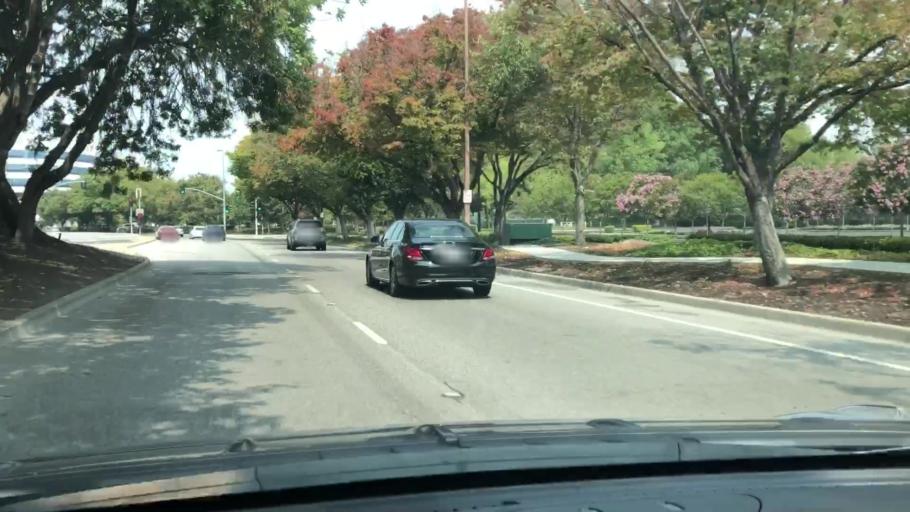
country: US
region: California
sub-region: Santa Clara County
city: Santa Clara
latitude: 37.3914
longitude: -121.9730
